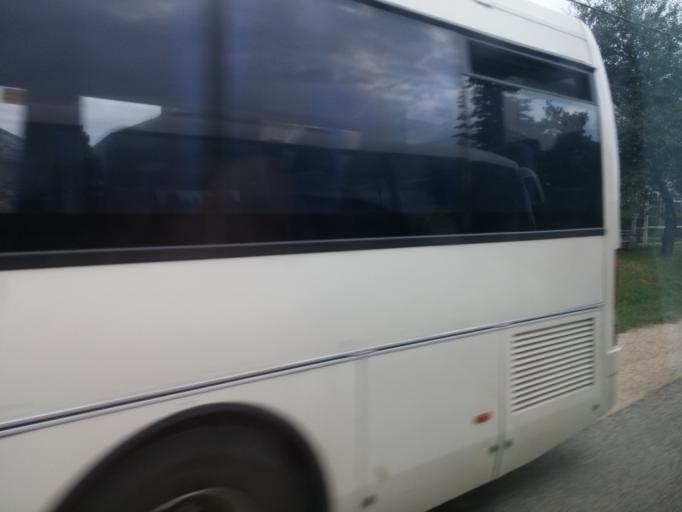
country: HU
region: Fejer
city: Bakonycsernye
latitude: 47.2641
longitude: 18.0415
